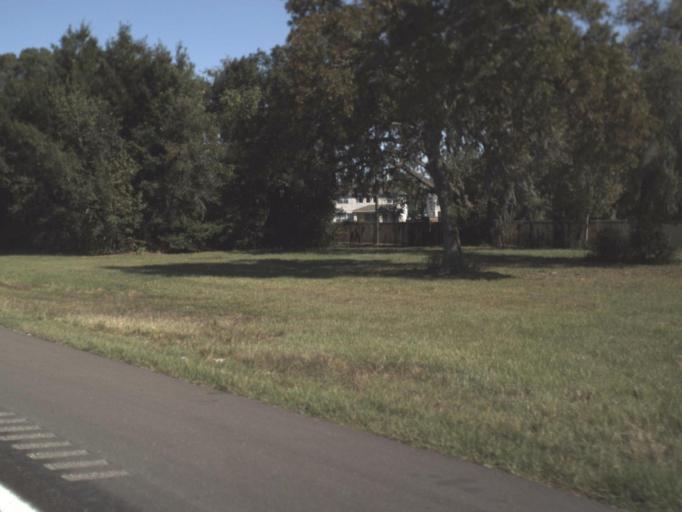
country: US
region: Florida
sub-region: Hernando County
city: Masaryktown
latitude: 28.4432
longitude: -82.4849
